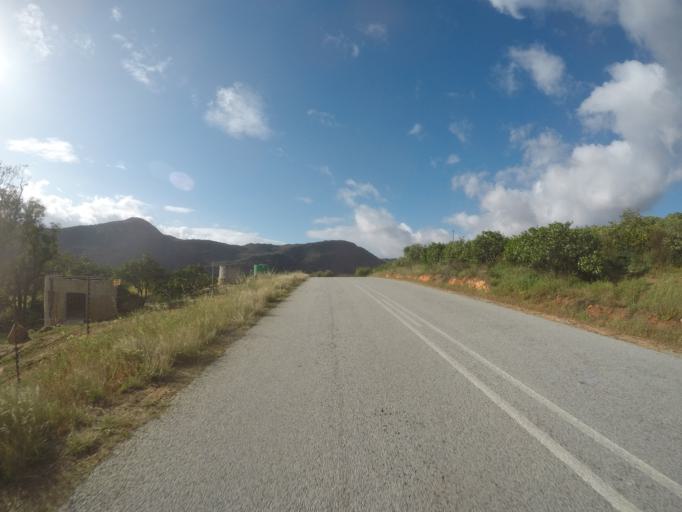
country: ZA
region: Western Cape
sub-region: West Coast District Municipality
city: Clanwilliam
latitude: -32.4364
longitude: 18.9396
